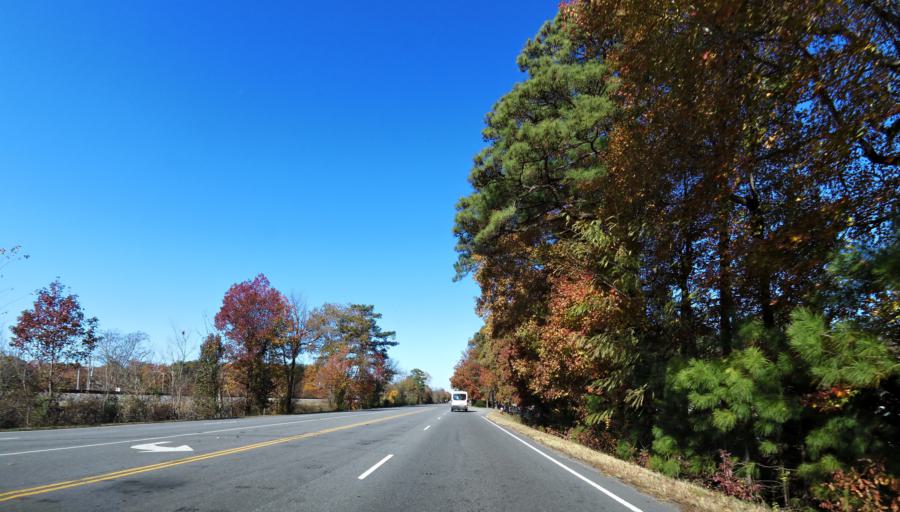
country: US
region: Virginia
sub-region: City of Williamsburg
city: Williamsburg
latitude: 37.2442
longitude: -76.6522
